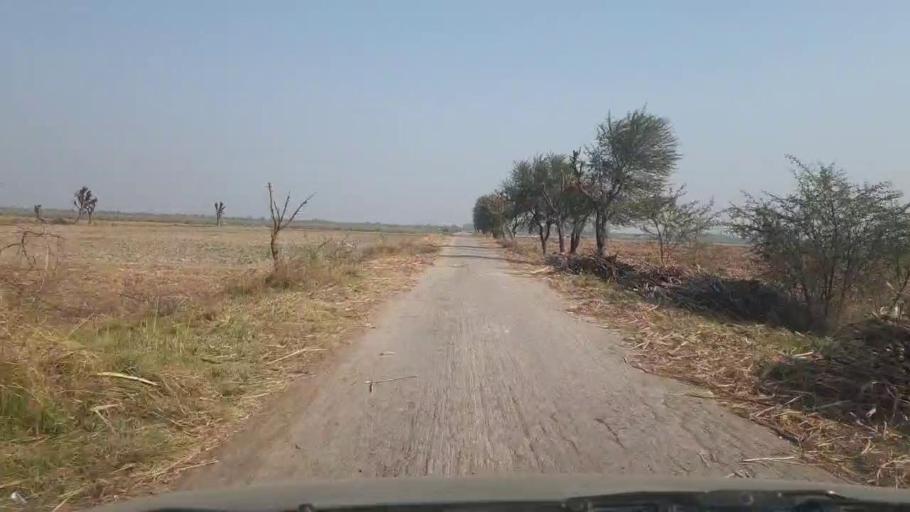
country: PK
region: Sindh
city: Mirwah Gorchani
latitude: 25.2666
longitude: 69.1643
